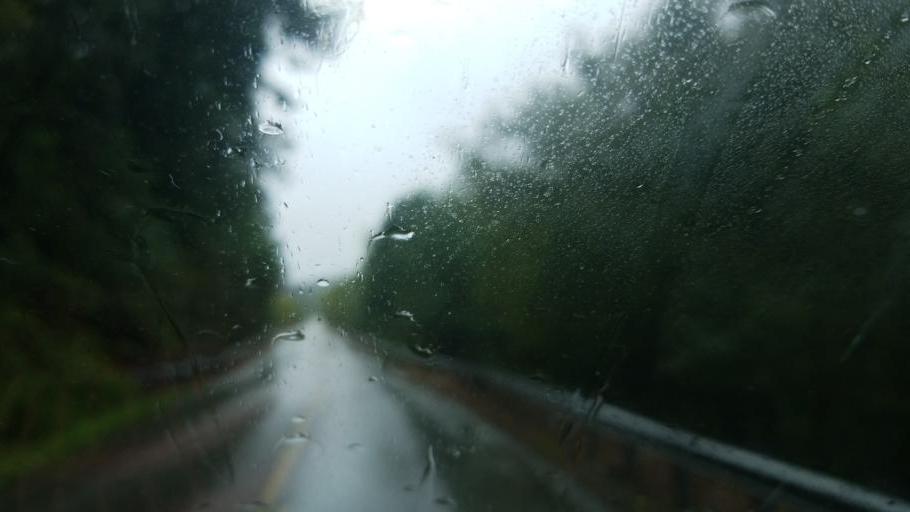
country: US
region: Kentucky
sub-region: Greenup County
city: South Shore
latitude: 38.7003
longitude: -82.9432
